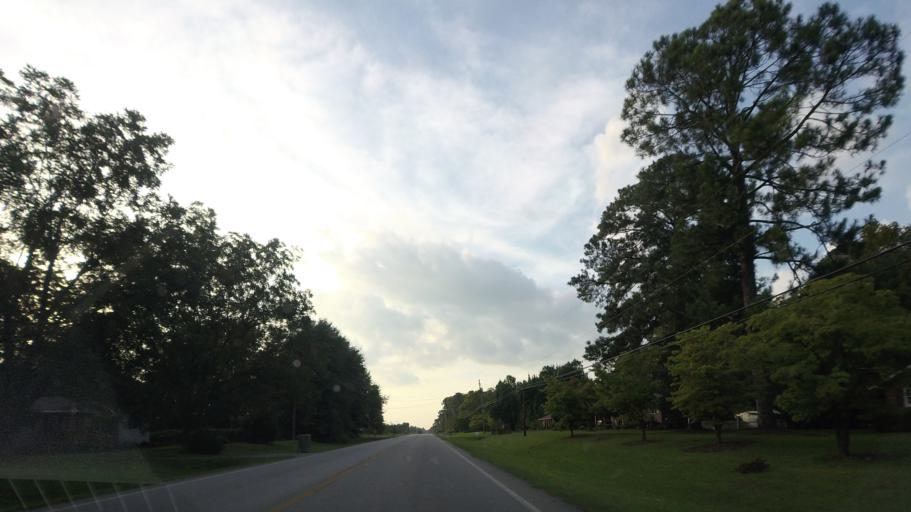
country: US
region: Georgia
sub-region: Wilkinson County
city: Gordon
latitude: 32.8876
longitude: -83.3493
